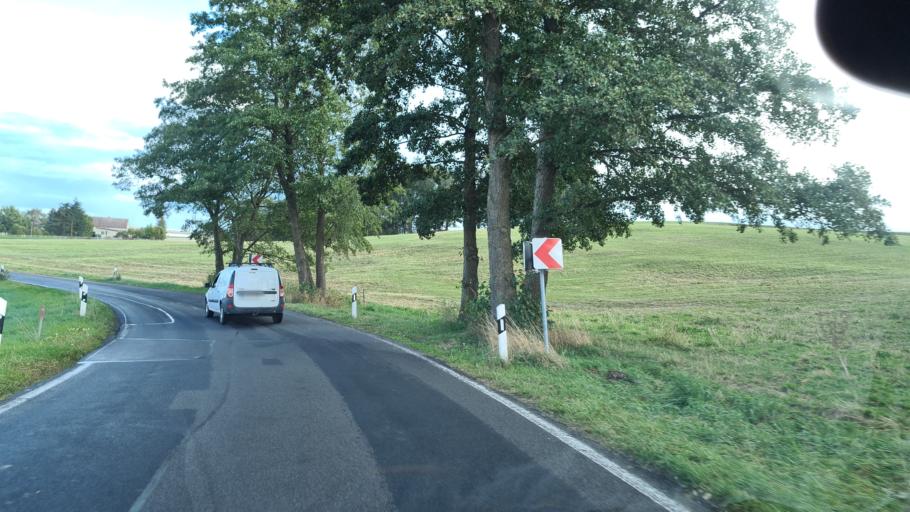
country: DE
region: Saxony
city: Dahlen
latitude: 51.3611
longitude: 13.0334
